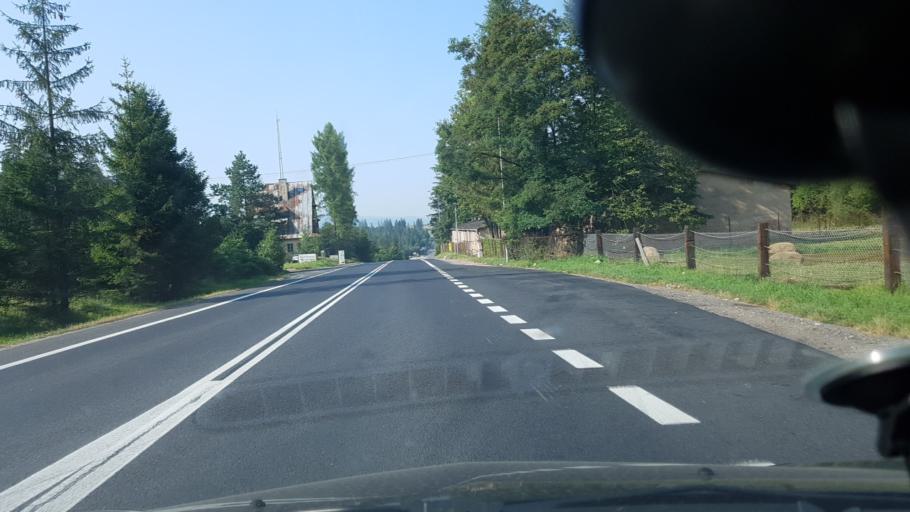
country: PL
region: Lesser Poland Voivodeship
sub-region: Powiat nowotarski
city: Chyzne
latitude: 49.4120
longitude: 19.6626
